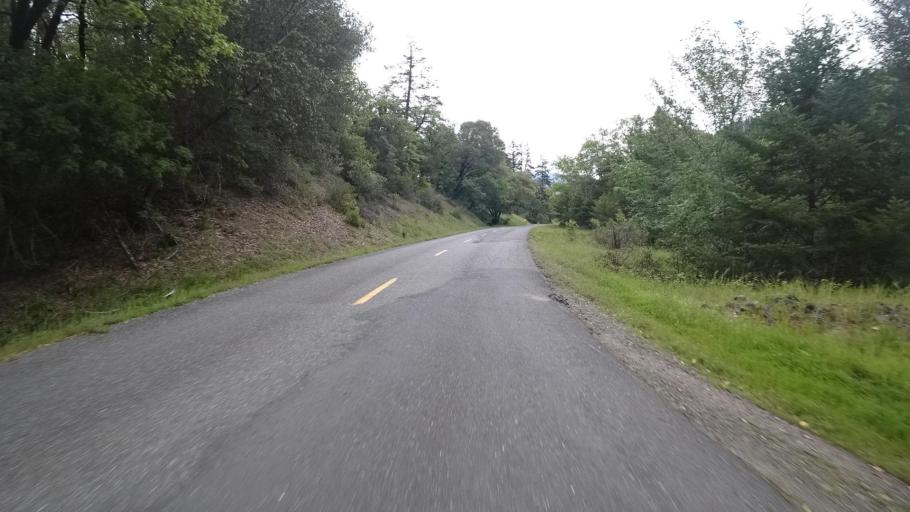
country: US
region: California
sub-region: Humboldt County
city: Redway
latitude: 40.2246
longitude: -123.6057
